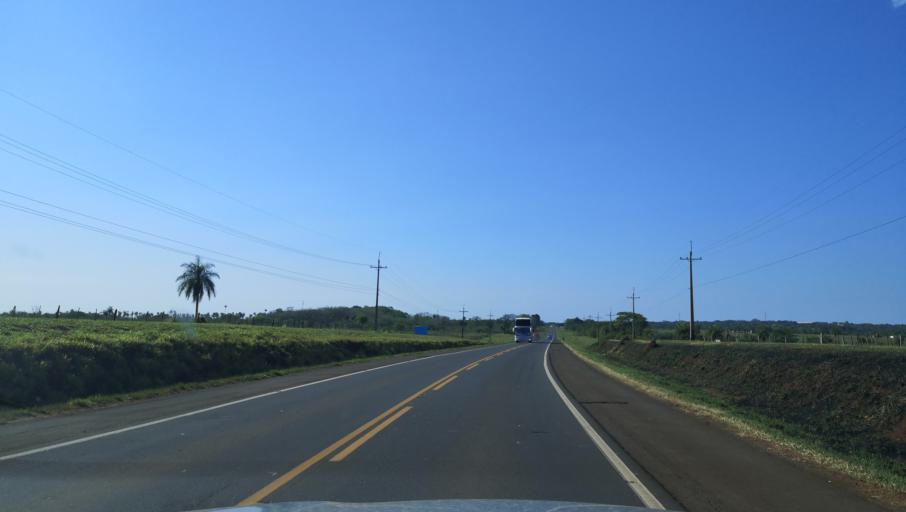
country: PY
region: Misiones
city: Santa Rosa
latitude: -26.9145
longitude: -56.8593
